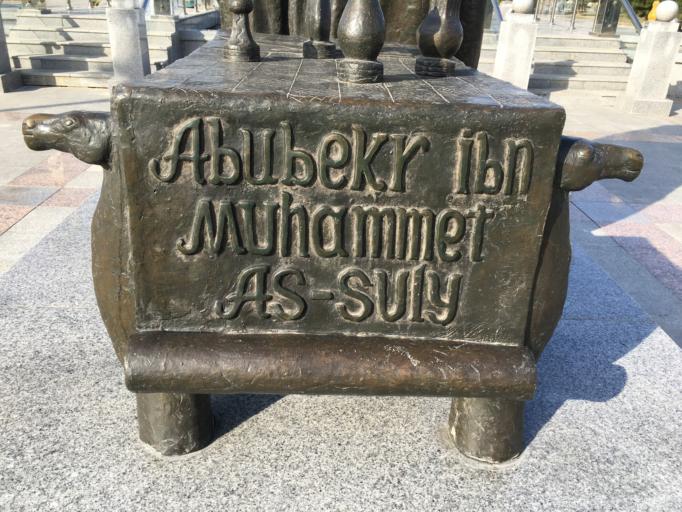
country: TM
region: Ahal
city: Ashgabat
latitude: 37.9414
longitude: 58.3767
